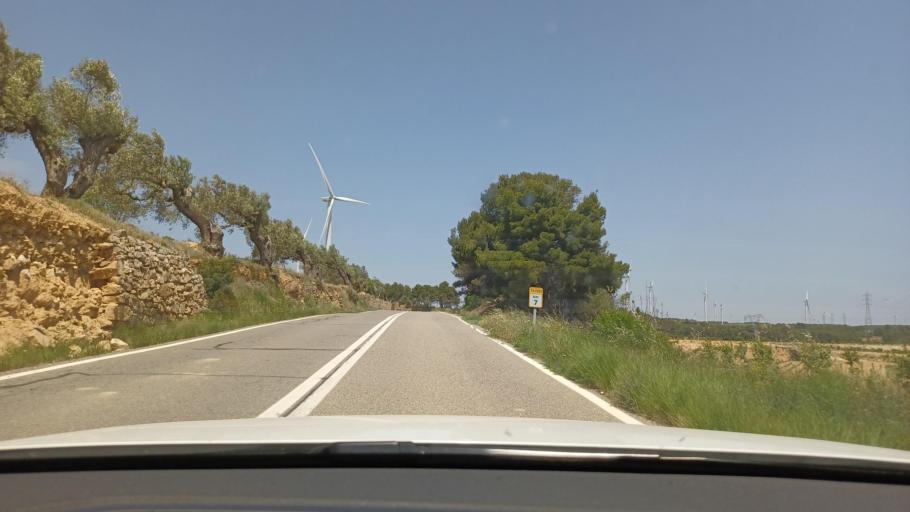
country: ES
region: Catalonia
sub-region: Provincia de Tarragona
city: Vilalba dels Arcs
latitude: 41.1023
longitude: 0.4172
